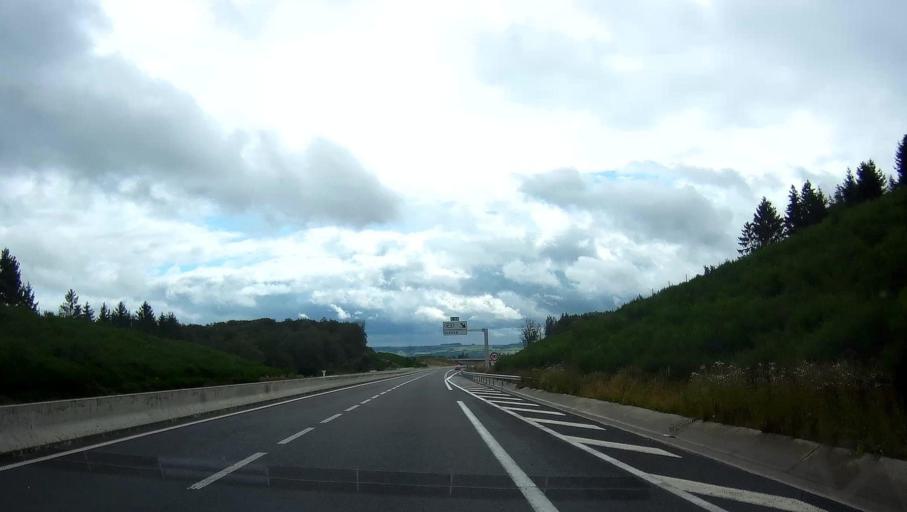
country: FR
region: Champagne-Ardenne
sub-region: Departement des Ardennes
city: Rimogne
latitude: 49.8510
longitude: 4.5132
